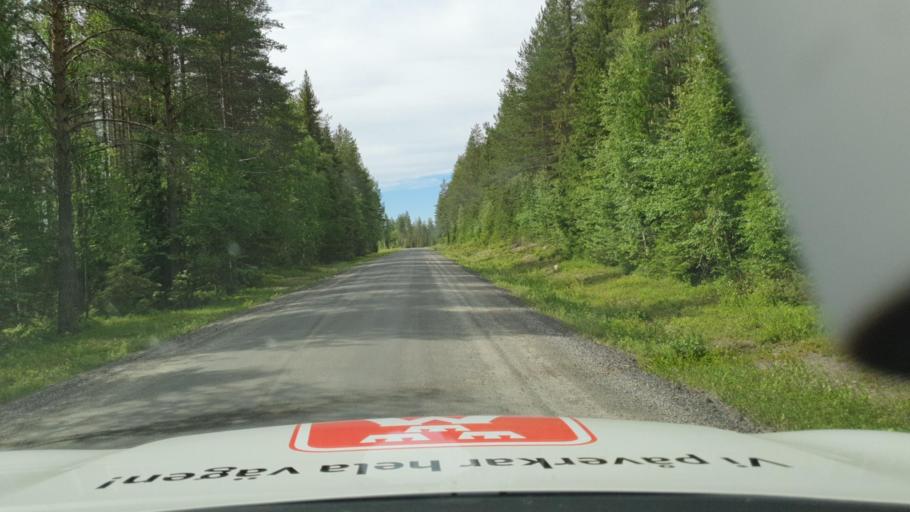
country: SE
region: Vaesterbotten
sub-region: Skelleftea Kommun
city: Burtraesk
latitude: 64.3836
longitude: 20.2813
